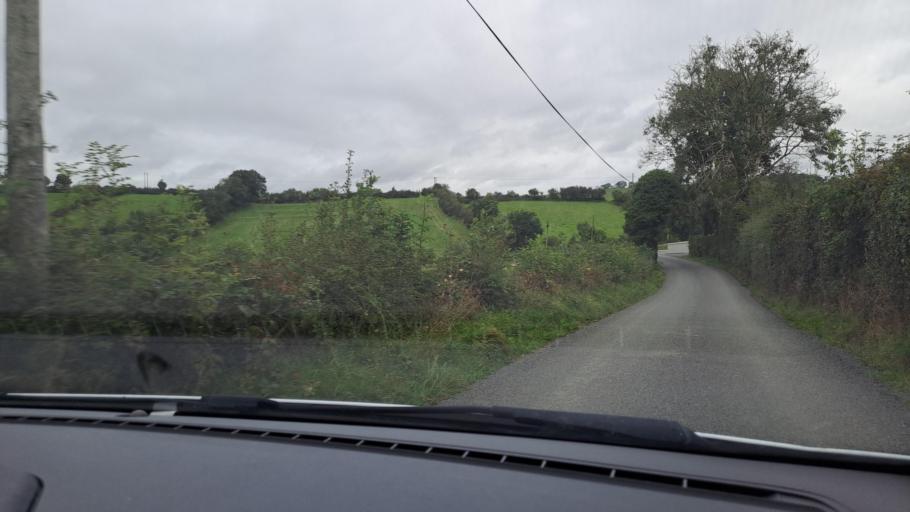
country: IE
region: Ulster
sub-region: County Monaghan
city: Castleblayney
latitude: 54.0415
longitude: -6.8001
